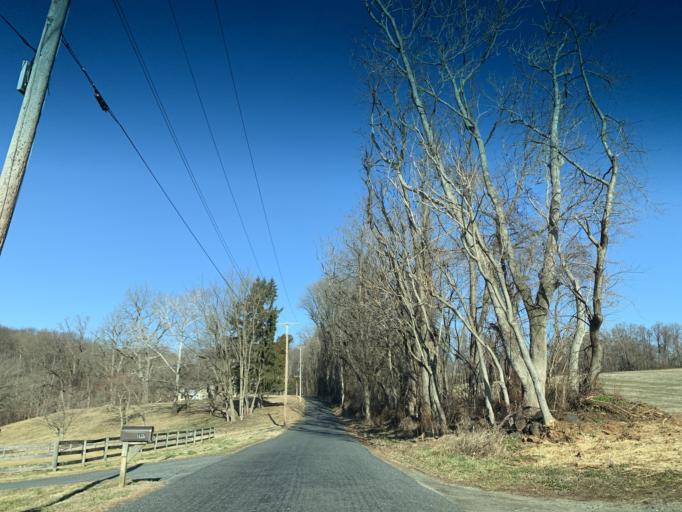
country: US
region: Maryland
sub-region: Harford County
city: South Bel Air
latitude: 39.6198
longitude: -76.2616
